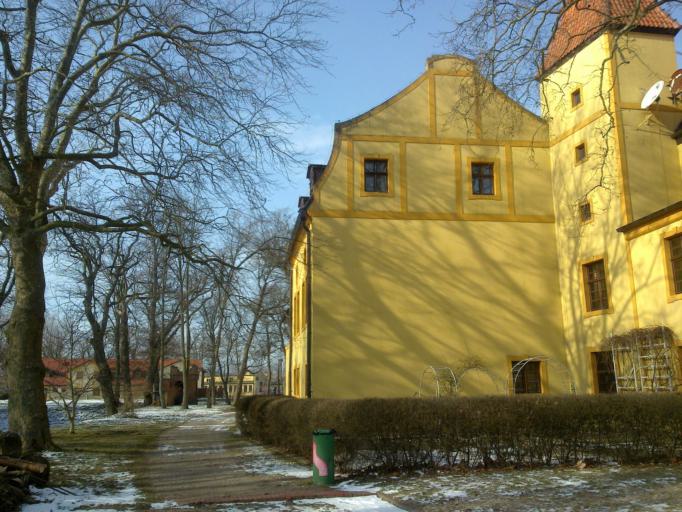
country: PL
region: Pomeranian Voivodeship
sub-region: Powiat pucki
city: Krokowa
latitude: 54.7767
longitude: 18.1641
